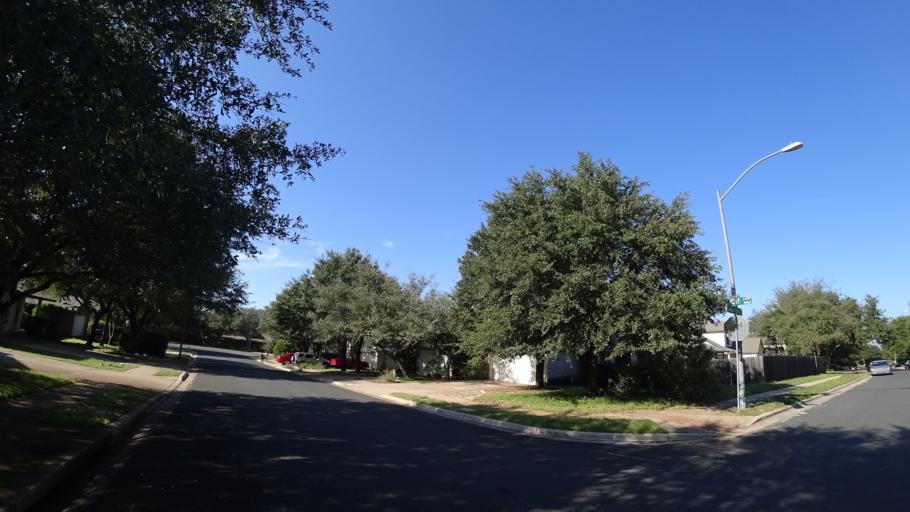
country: US
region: Texas
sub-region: Travis County
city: Shady Hollow
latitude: 30.2013
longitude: -97.8543
